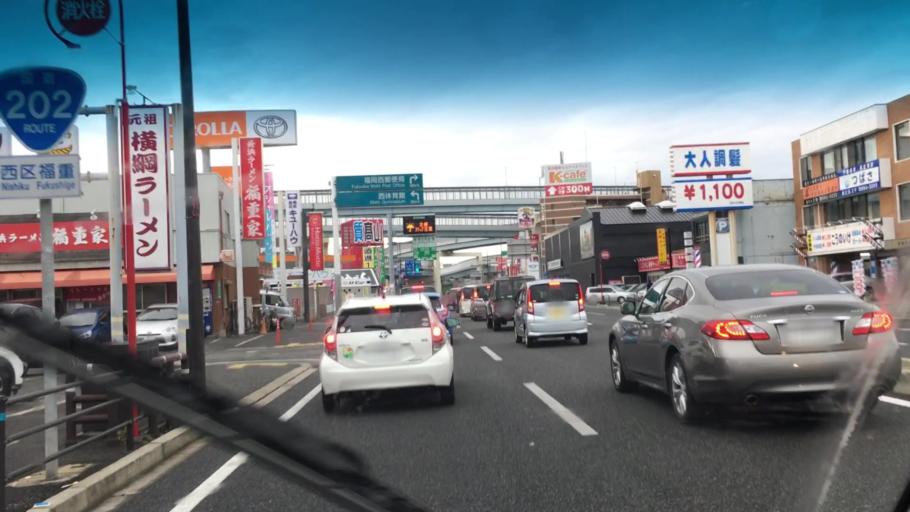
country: JP
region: Fukuoka
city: Fukuoka-shi
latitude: 33.5682
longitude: 130.3203
